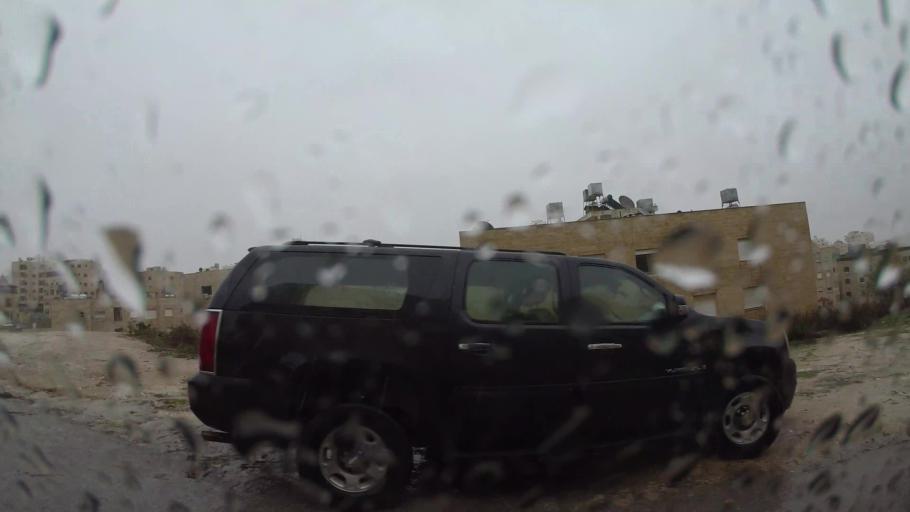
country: JO
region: Amman
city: Al Jubayhah
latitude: 32.0130
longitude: 35.8918
